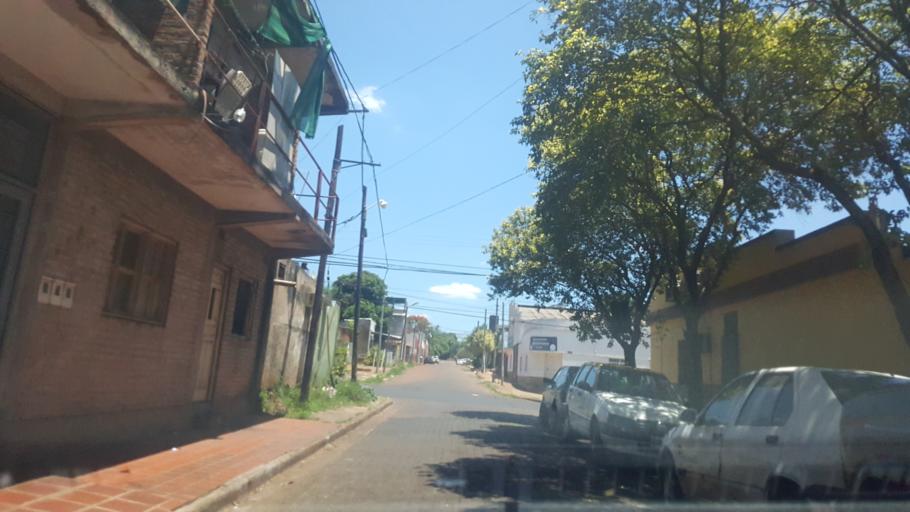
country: AR
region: Misiones
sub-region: Departamento de Capital
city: Posadas
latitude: -27.3699
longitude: -55.9044
